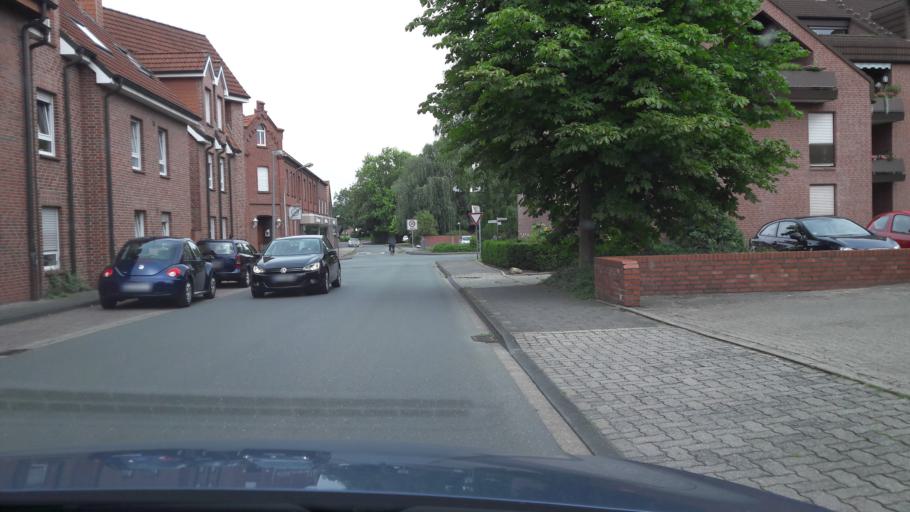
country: DE
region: North Rhine-Westphalia
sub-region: Regierungsbezirk Munster
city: Ennigerloh
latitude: 51.8375
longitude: 8.0229
